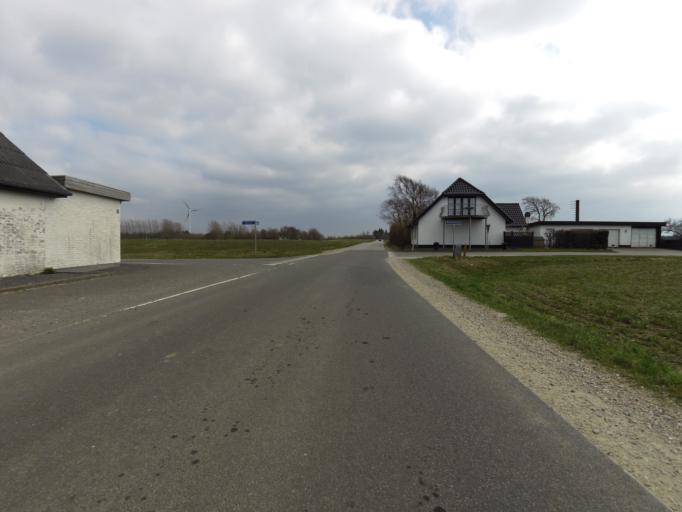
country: DK
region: Central Jutland
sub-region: Holstebro Kommune
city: Holstebro
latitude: 56.4310
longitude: 8.6834
